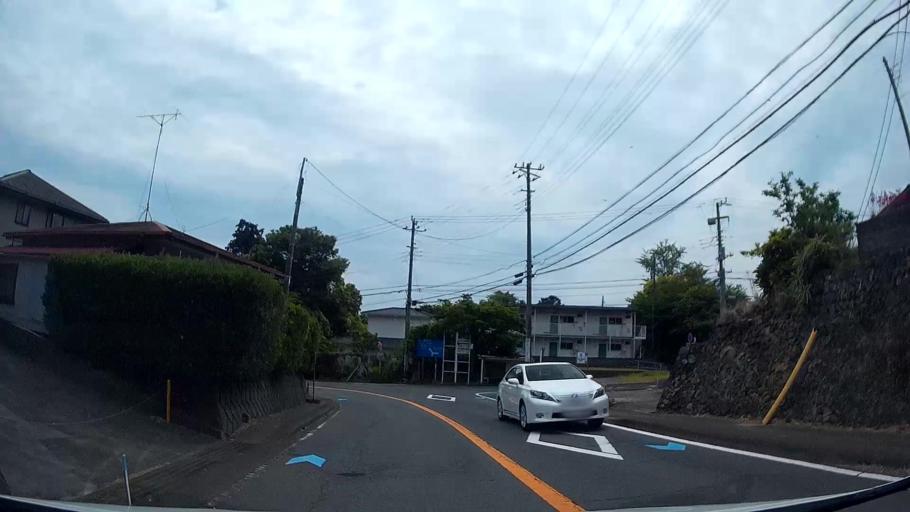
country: JP
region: Shizuoka
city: Ito
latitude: 34.9093
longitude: 139.1345
